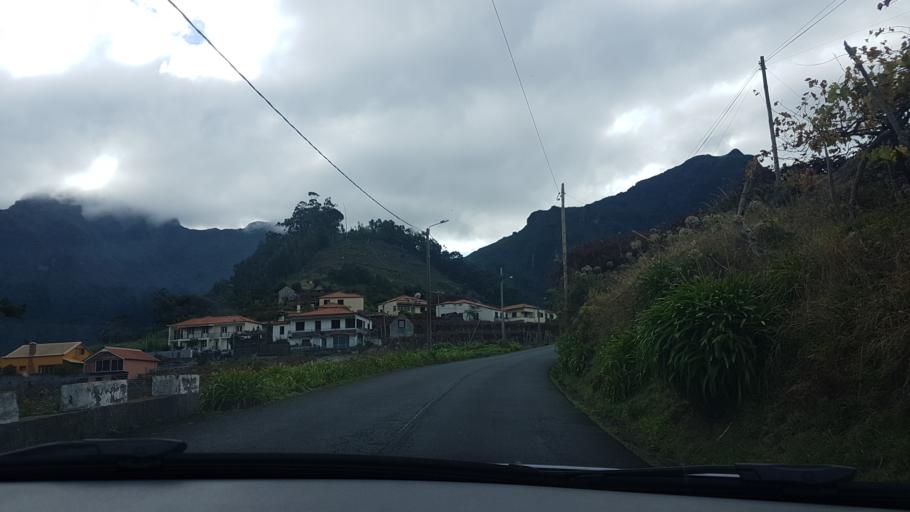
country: PT
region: Madeira
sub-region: Sao Vicente
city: Sao Vicente
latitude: 32.7804
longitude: -17.0294
